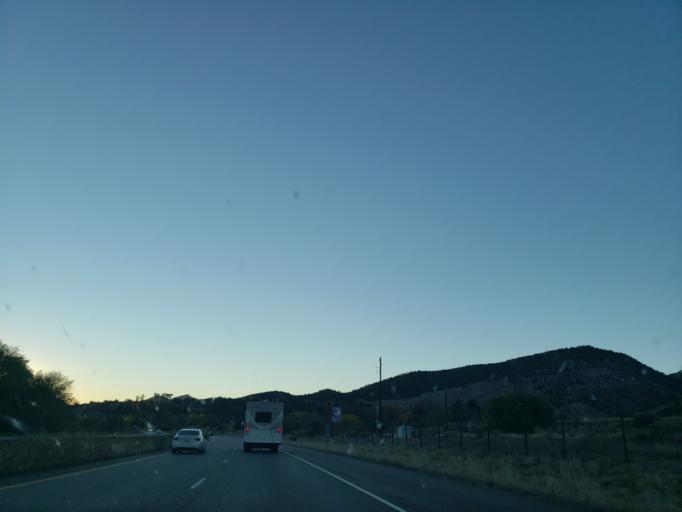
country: US
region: Colorado
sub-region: Garfield County
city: New Castle
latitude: 39.5734
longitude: -107.4676
